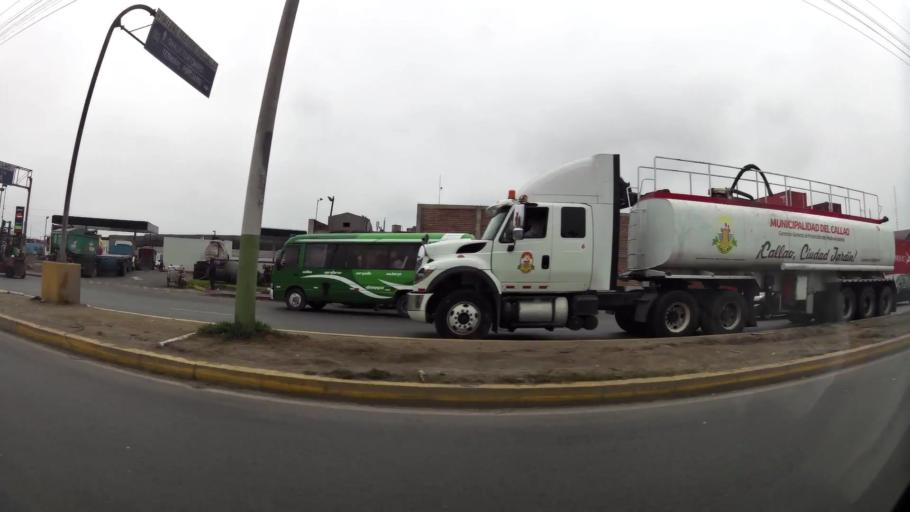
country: PE
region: Callao
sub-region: Callao
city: Callao
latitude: -12.0498
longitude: -77.1260
